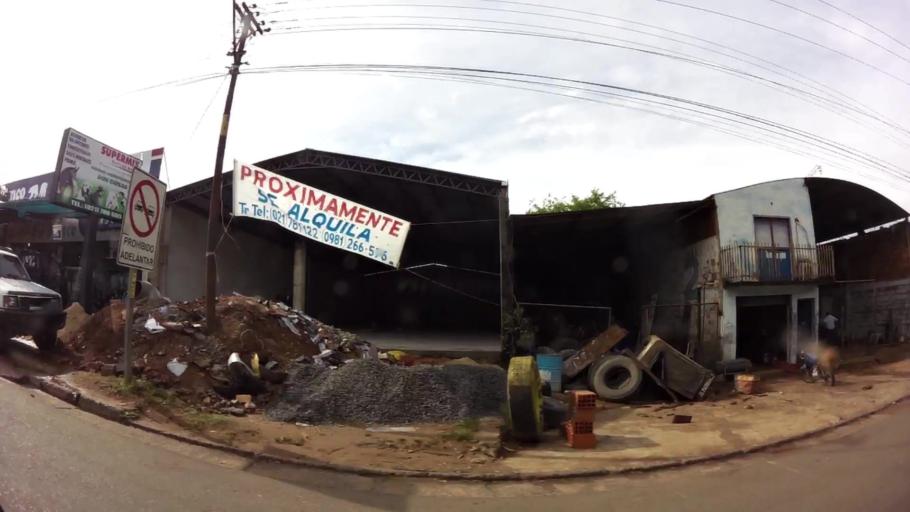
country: PY
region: Central
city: Limpio
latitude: -25.1665
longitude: -57.4693
